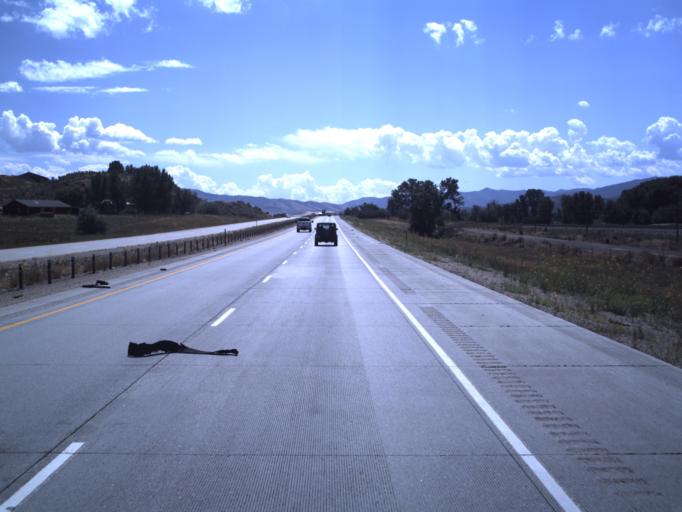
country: US
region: Utah
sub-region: Morgan County
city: Mountain Green
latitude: 41.0915
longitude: -111.7371
